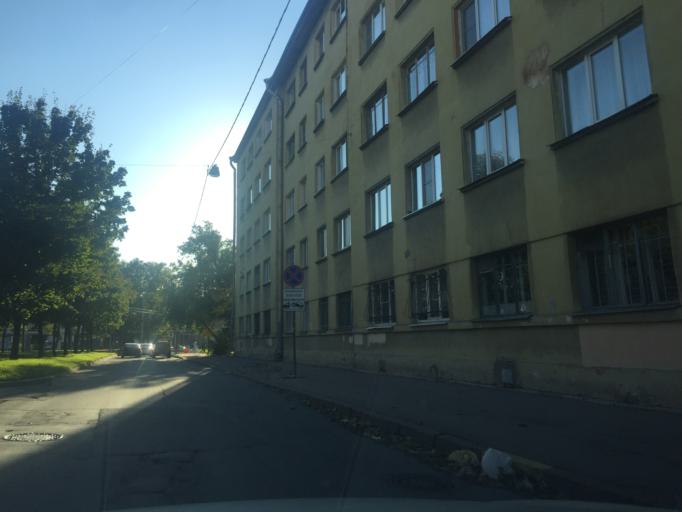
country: RU
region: Leningrad
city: Sampsonievskiy
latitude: 59.9788
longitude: 30.3466
